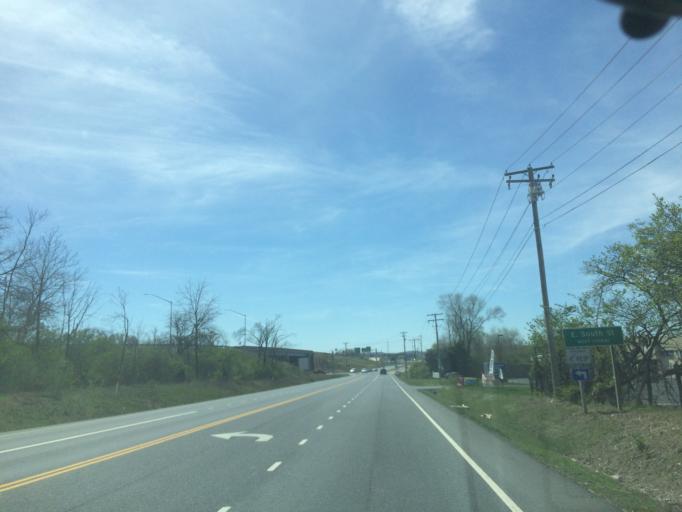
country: US
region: Maryland
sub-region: Frederick County
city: Frederick
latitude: 39.4054
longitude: -77.3914
